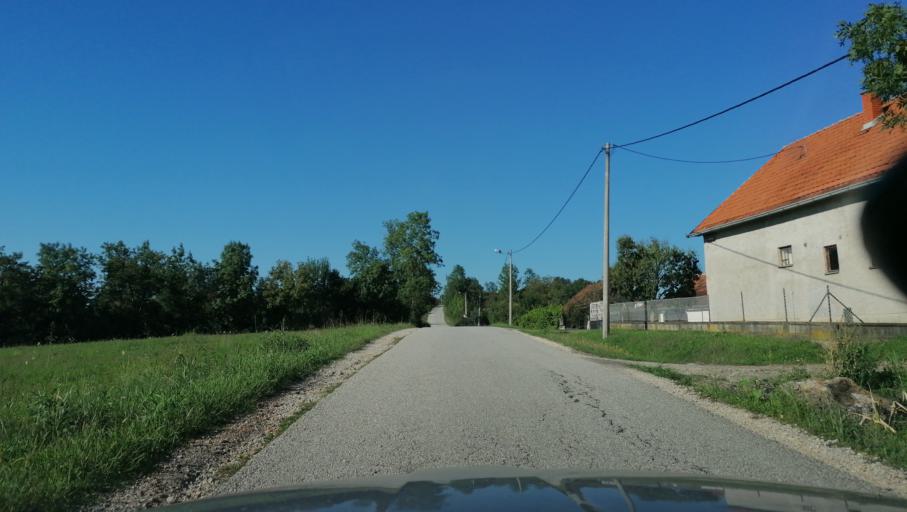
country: RS
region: Central Serbia
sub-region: Sumadijski Okrug
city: Knic
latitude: 43.8674
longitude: 20.6057
